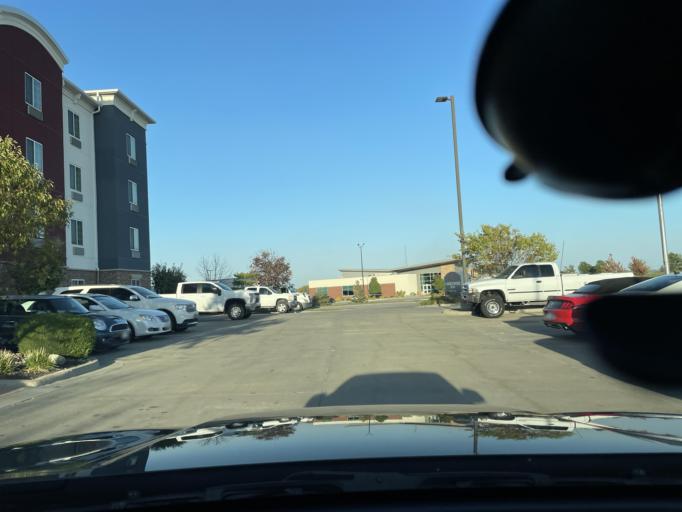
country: US
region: Missouri
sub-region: Andrew County
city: Country Club Village
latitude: 39.8166
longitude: -94.8110
